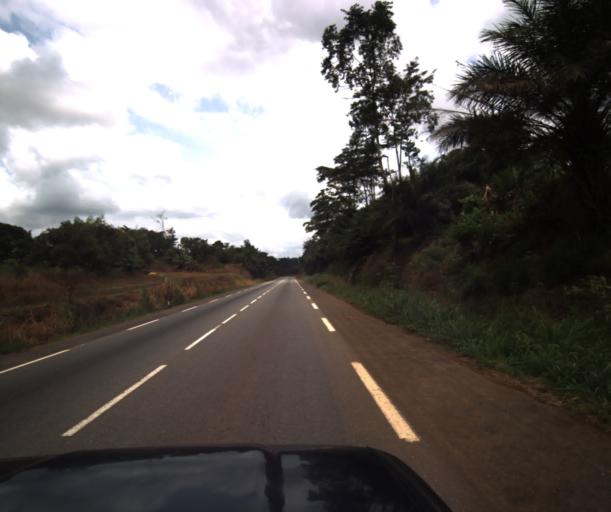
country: CM
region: Centre
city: Eseka
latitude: 3.8481
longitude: 10.9720
